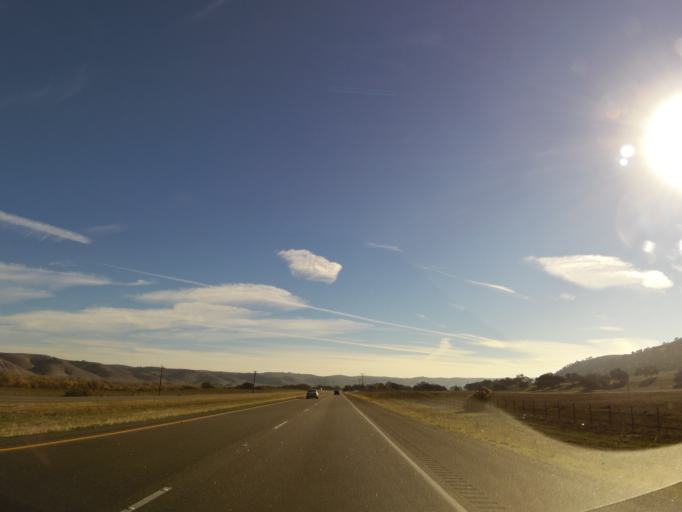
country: US
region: California
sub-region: San Luis Obispo County
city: San Miguel
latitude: 35.8531
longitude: -120.7799
